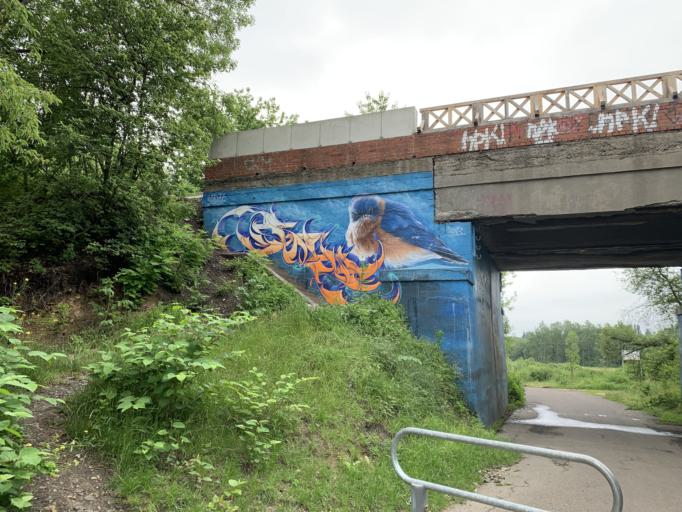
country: PL
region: Silesian Voivodeship
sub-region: Bytom
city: Bytom
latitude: 50.3290
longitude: 18.9502
